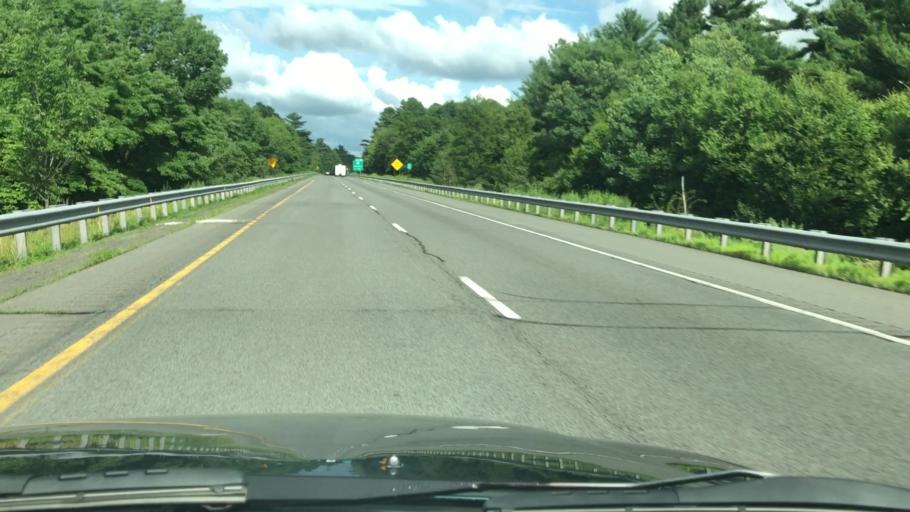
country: US
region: Pennsylvania
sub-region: Pike County
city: Gold Key Lake
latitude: 41.3403
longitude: -74.8818
